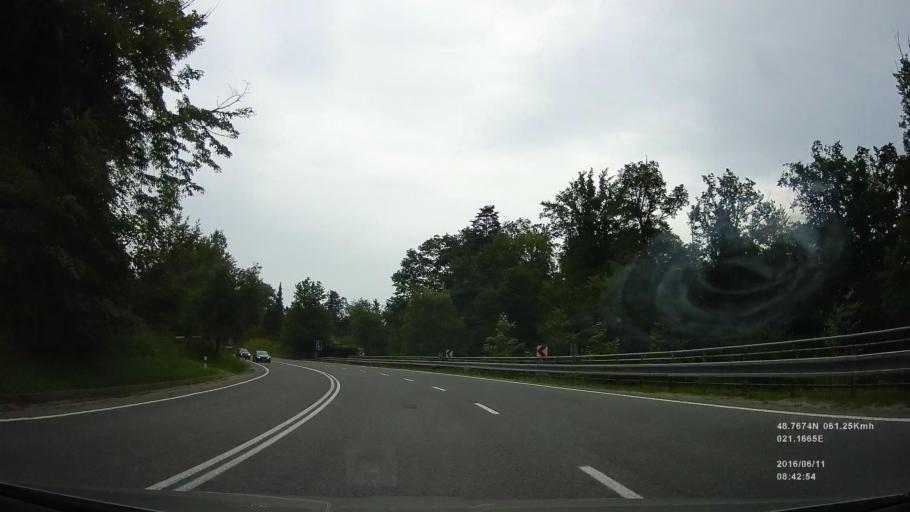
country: SK
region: Kosicky
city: Kosice
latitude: 48.7524
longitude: 21.2213
